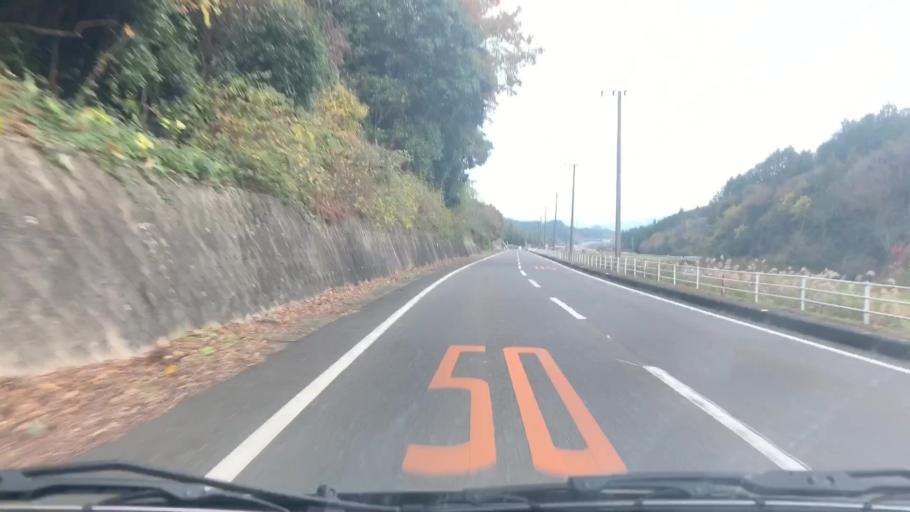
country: JP
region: Saga Prefecture
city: Ureshinomachi-shimojuku
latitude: 33.1174
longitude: 129.9773
